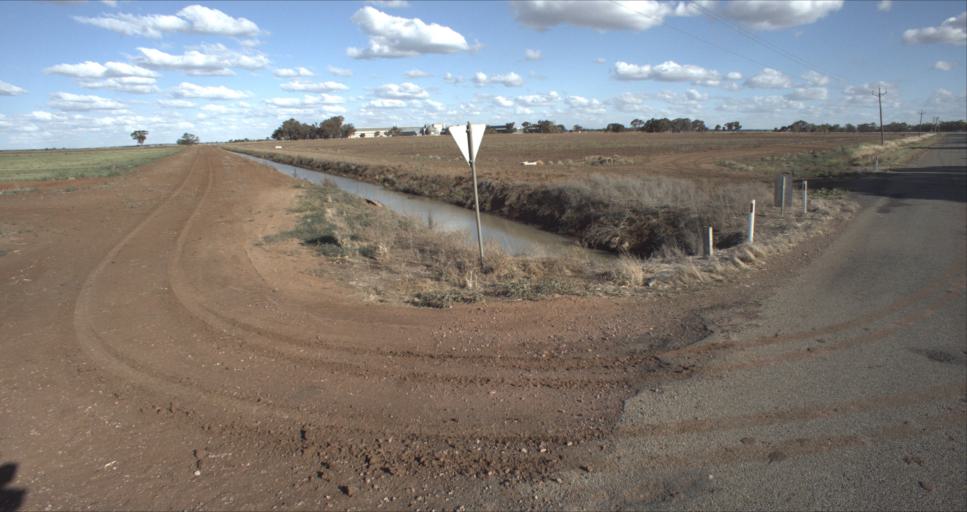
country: AU
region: New South Wales
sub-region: Leeton
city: Leeton
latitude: -34.5492
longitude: 146.2793
